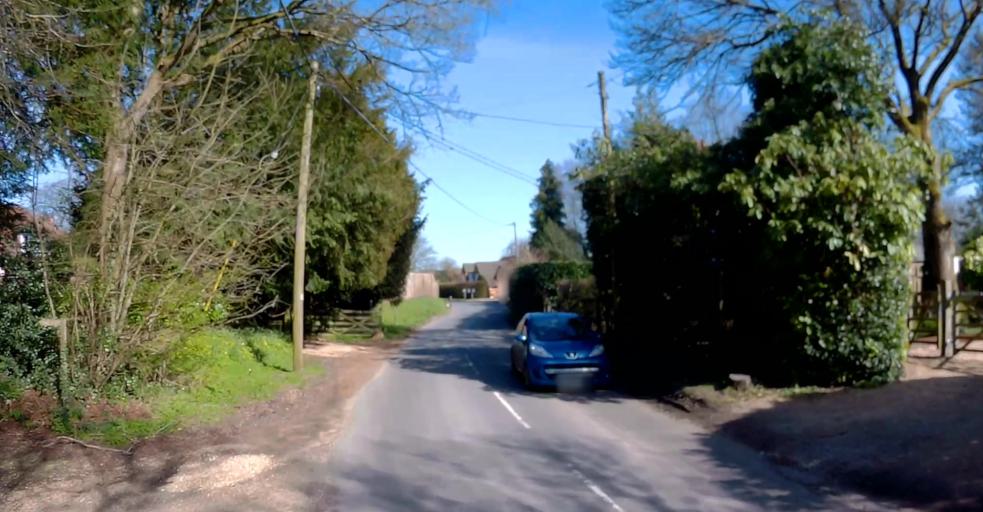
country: GB
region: England
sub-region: Hampshire
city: Four Marks
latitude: 51.1565
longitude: -1.0486
